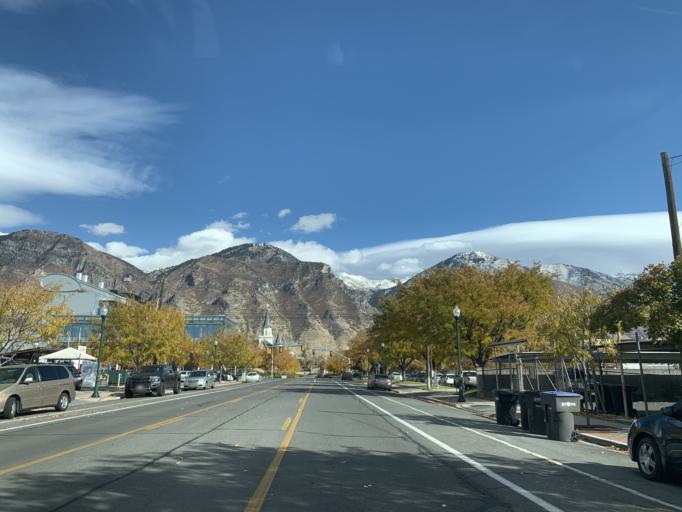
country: US
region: Utah
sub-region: Utah County
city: Provo
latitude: 40.2323
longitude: -111.6637
